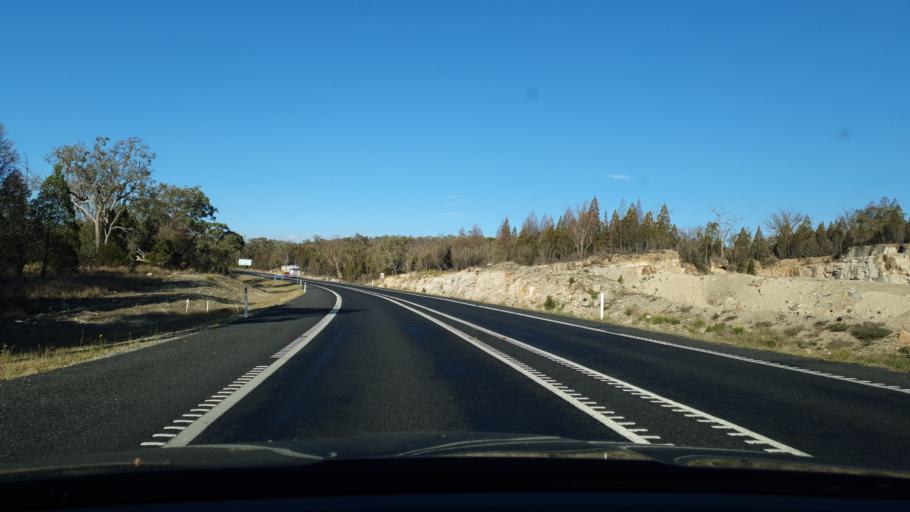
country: AU
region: Queensland
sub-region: Southern Downs
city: Stanthorpe
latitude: -28.6835
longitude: 151.9172
